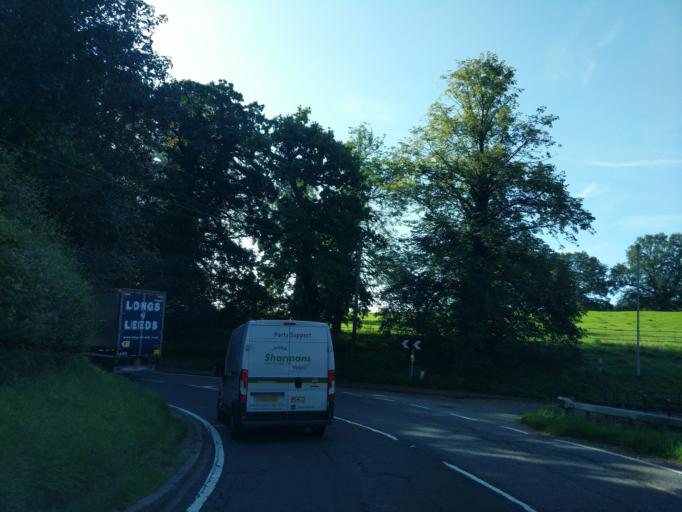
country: GB
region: England
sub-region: Lincolnshire
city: Bourne
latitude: 52.7948
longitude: -0.4504
